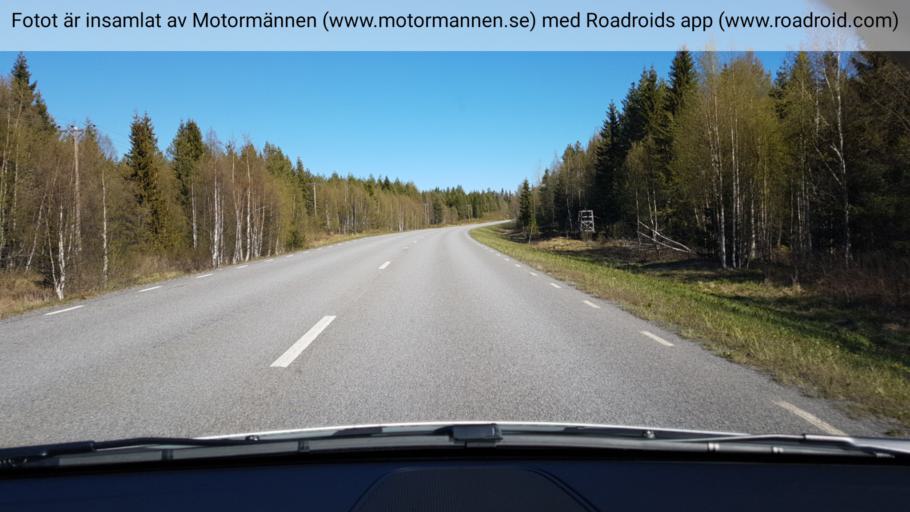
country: SE
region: Jaemtland
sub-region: Stroemsunds Kommun
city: Stroemsund
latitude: 64.3047
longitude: 15.2986
